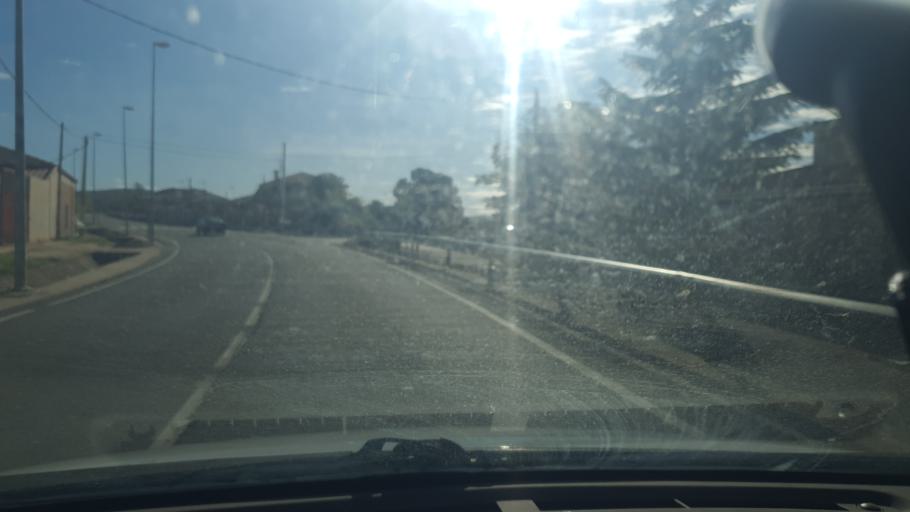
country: ES
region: Castille and Leon
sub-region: Provincia de Avila
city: Penalba de Avila
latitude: 40.7997
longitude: -4.7622
